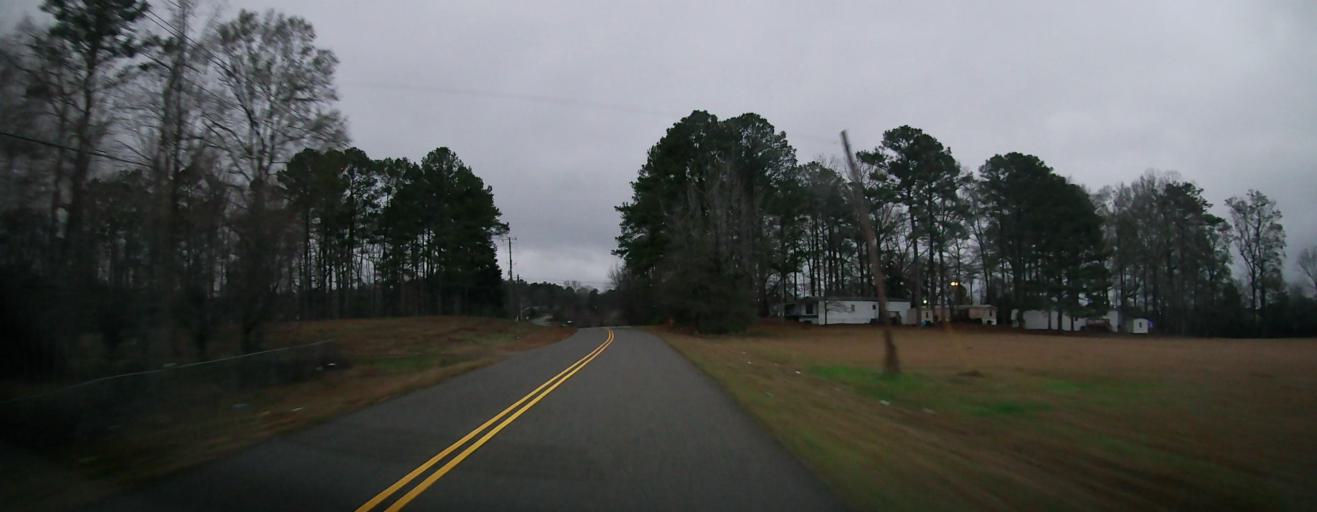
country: US
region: Alabama
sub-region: Tuscaloosa County
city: Vance
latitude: 33.1595
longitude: -87.2299
